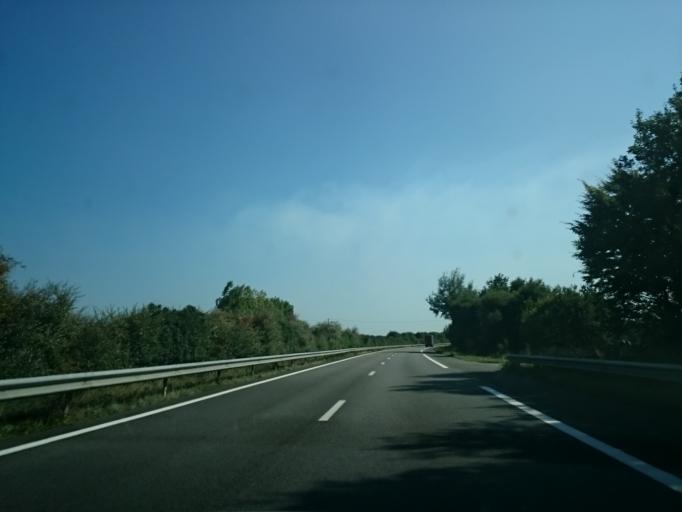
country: FR
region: Pays de la Loire
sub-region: Departement de la Loire-Atlantique
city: Jans
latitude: 47.6088
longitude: -1.6302
